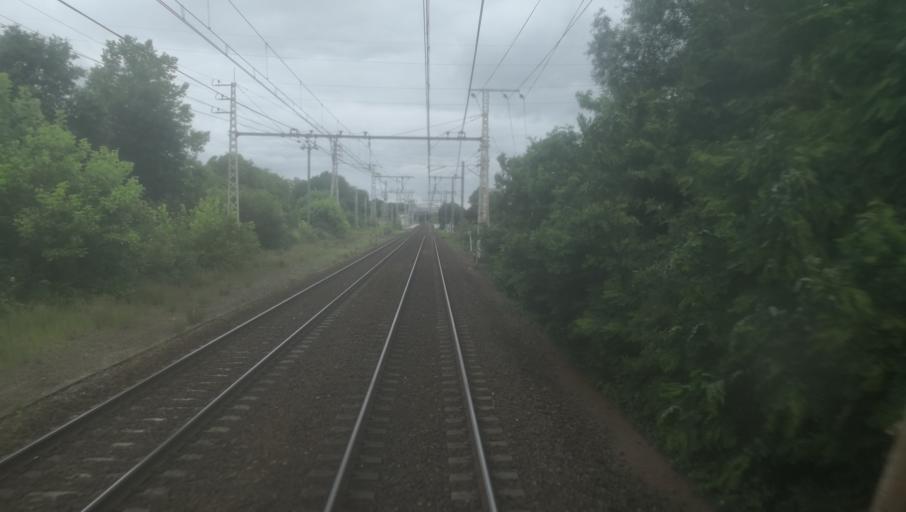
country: FR
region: Midi-Pyrenees
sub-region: Departement de la Haute-Garonne
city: Saint-Jory
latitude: 43.7359
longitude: 1.3735
